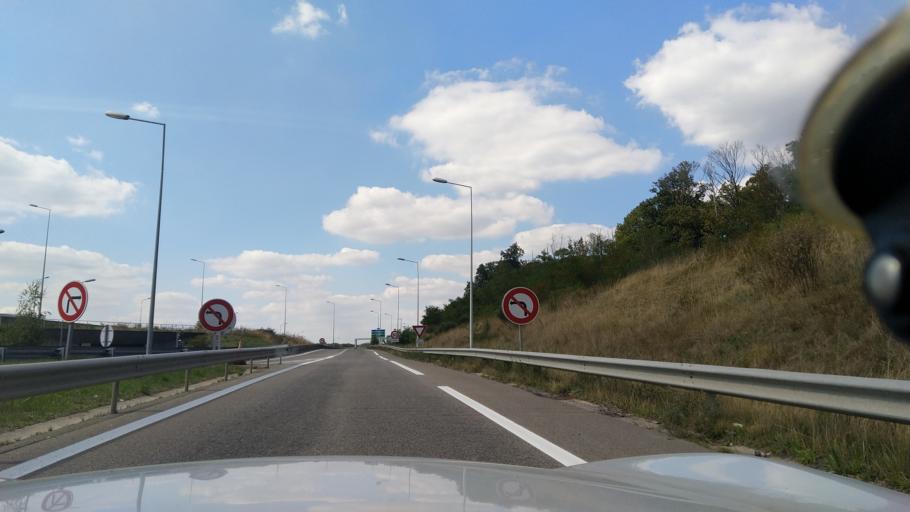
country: FR
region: Ile-de-France
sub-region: Departement des Yvelines
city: Viroflay
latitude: 48.7827
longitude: 2.1623
